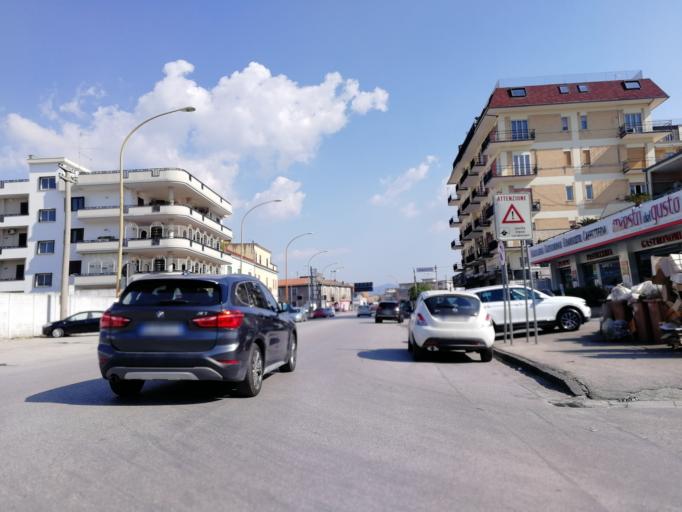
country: IT
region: Campania
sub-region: Provincia di Caserta
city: San Prisco
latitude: 41.0816
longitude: 14.2677
